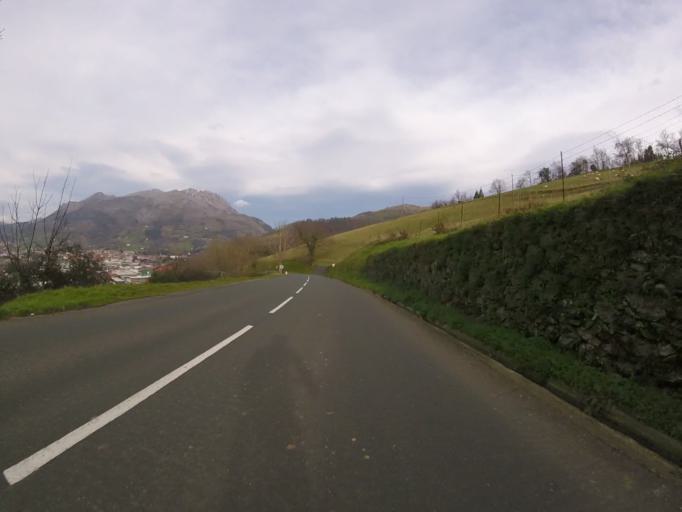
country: ES
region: Basque Country
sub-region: Provincia de Guipuzcoa
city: Azpeitia
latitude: 43.1707
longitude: -2.2457
